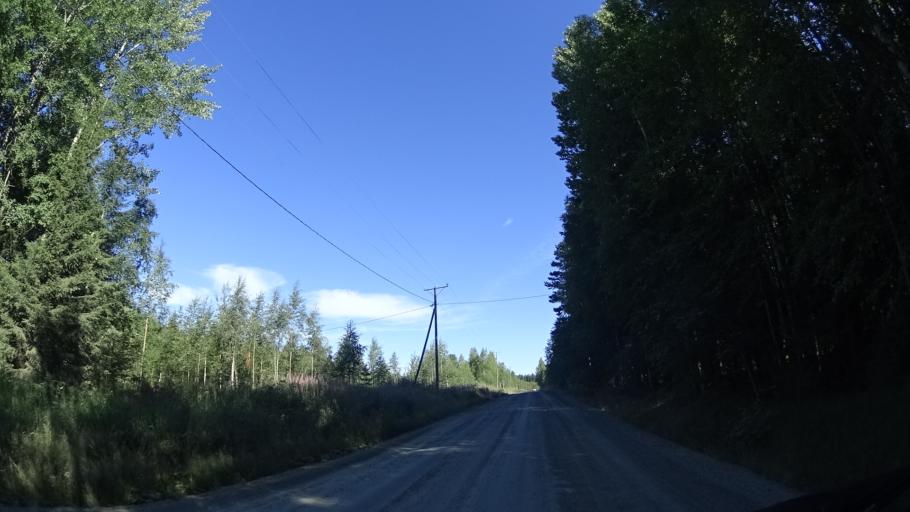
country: FI
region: Central Finland
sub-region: Jyvaeskylae
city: Petaejaevesi
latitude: 62.3434
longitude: 25.3341
